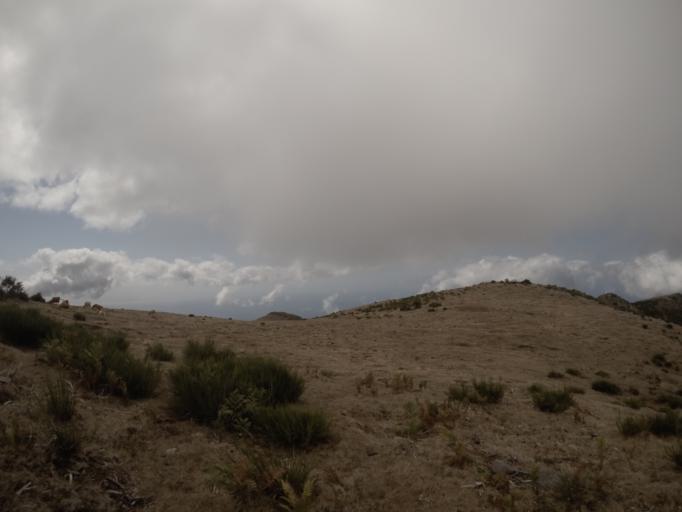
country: PT
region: Madeira
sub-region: Camara de Lobos
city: Curral das Freiras
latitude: 32.7162
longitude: -17.0024
